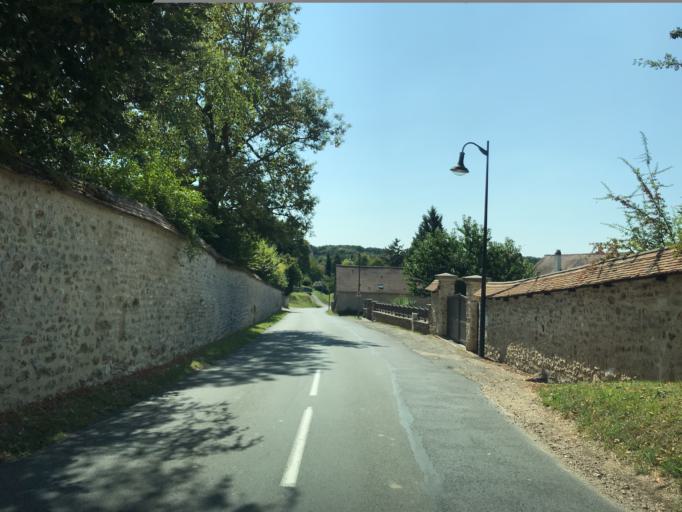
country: FR
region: Haute-Normandie
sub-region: Departement de l'Eure
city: La Chapelle-Reanville
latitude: 49.0967
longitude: 1.3787
